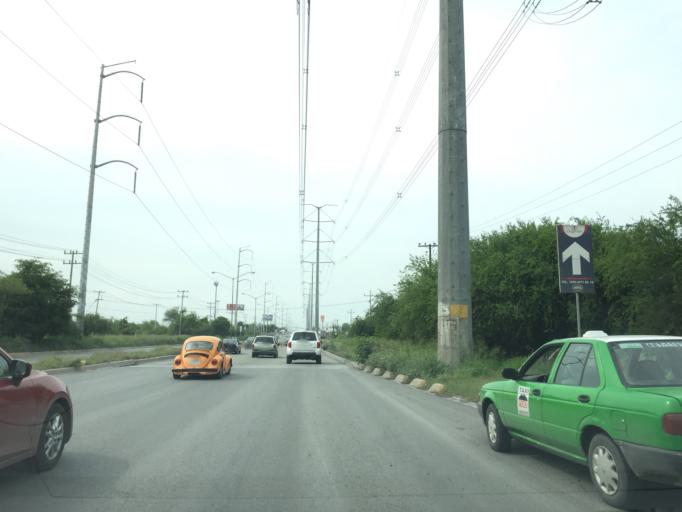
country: MX
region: Nuevo Leon
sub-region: Apodaca
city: Fraccionamiento Cosmopolis Octavo Sector
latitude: 25.7970
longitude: -100.2237
